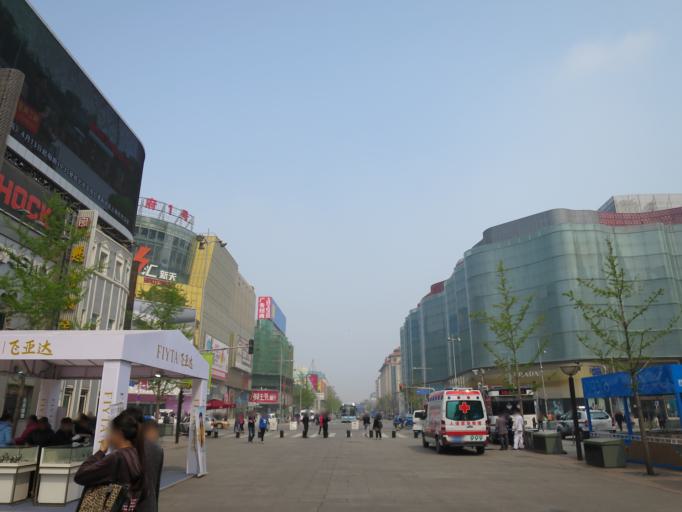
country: CN
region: Beijing
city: Beijing
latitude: 39.9136
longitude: 116.4051
